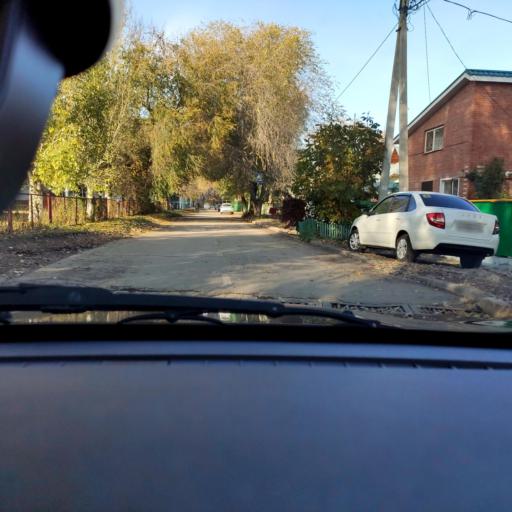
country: RU
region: Samara
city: Tol'yatti
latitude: 53.5265
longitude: 49.4022
